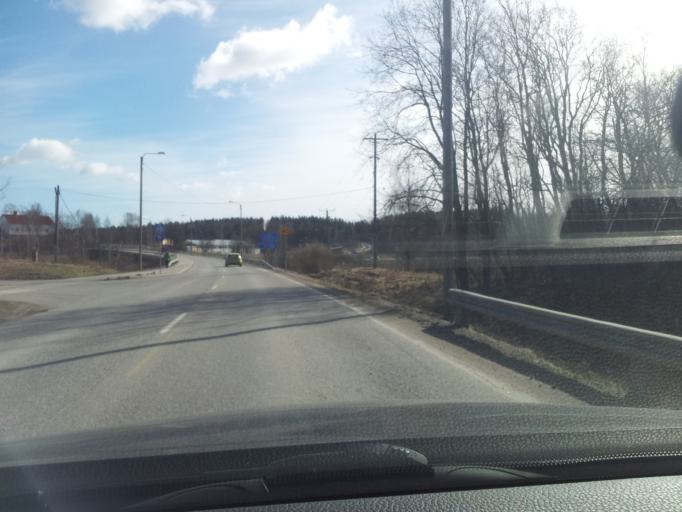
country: FI
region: Uusimaa
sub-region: Helsinki
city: Kirkkonummi
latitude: 60.1534
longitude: 24.5383
